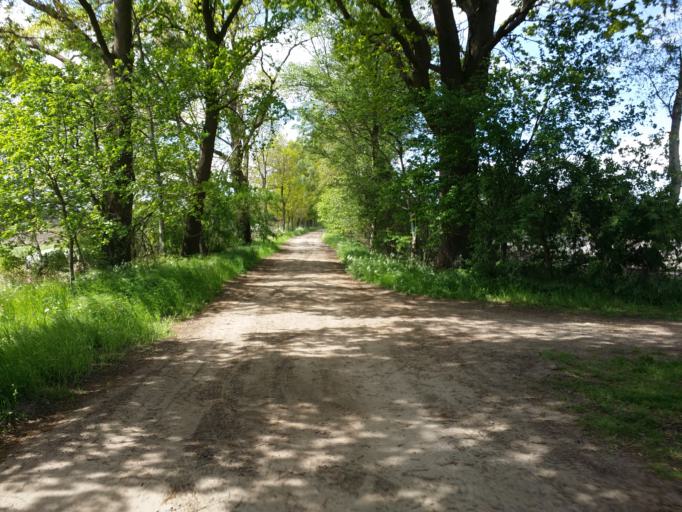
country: DE
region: Lower Saxony
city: Gross Ippener
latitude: 52.9845
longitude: 8.6306
